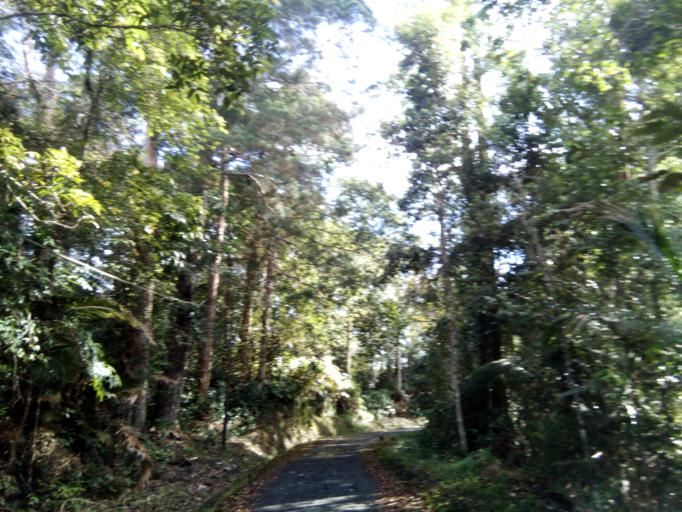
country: MY
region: Penang
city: Tanjung Tokong
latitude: 5.4188
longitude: 100.2520
